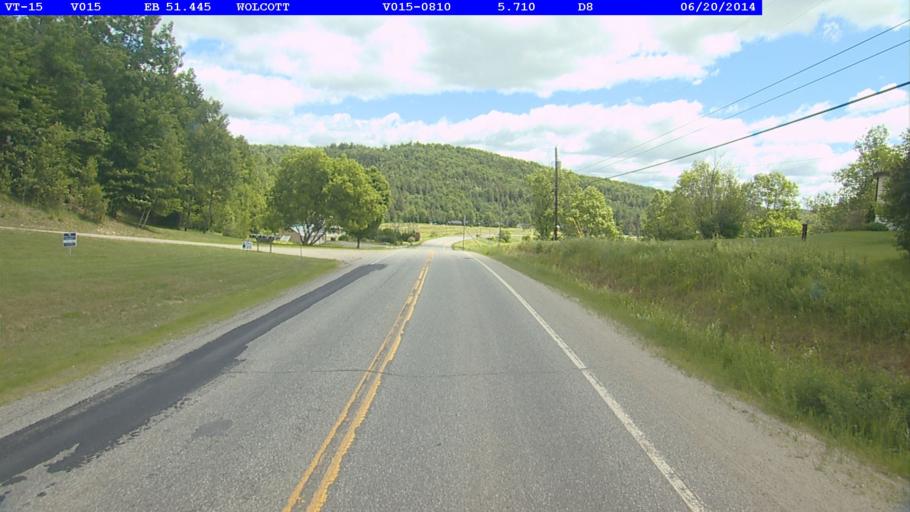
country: US
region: Vermont
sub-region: Caledonia County
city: Hardwick
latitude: 44.5338
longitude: -72.4389
